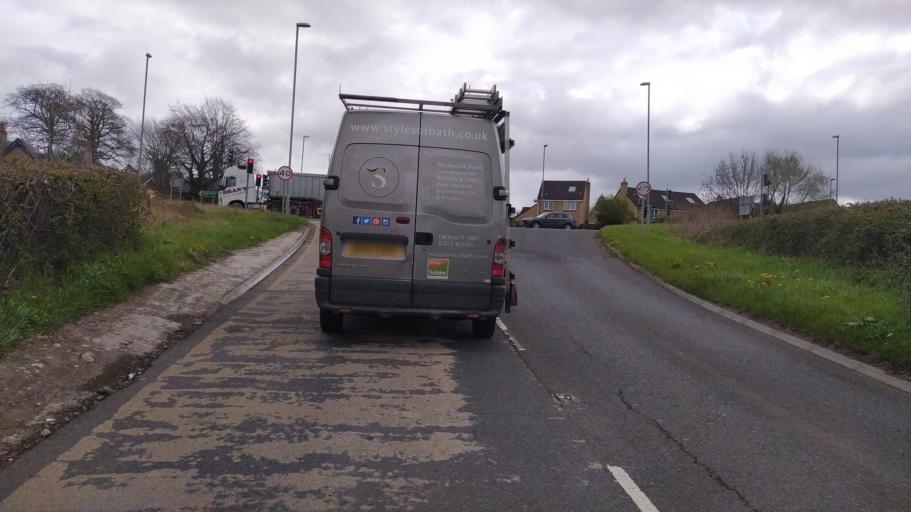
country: GB
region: England
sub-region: Wiltshire
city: North Bradley
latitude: 51.3017
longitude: -2.1784
